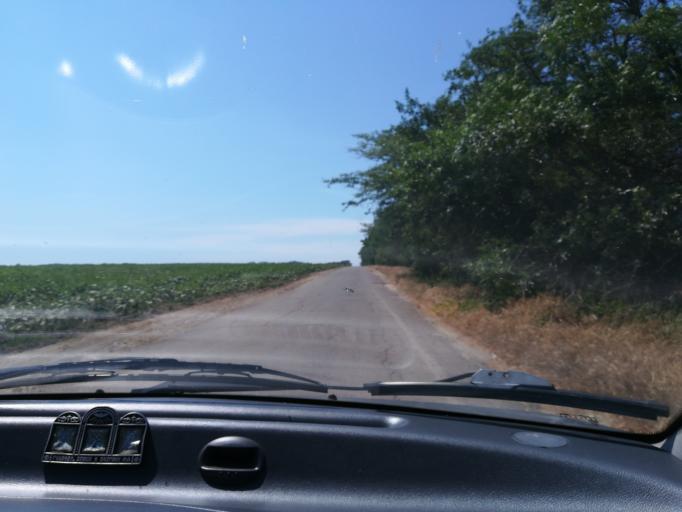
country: RU
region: Krasnodarskiy
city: Blagovetschenskaya
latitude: 45.0566
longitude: 37.1098
